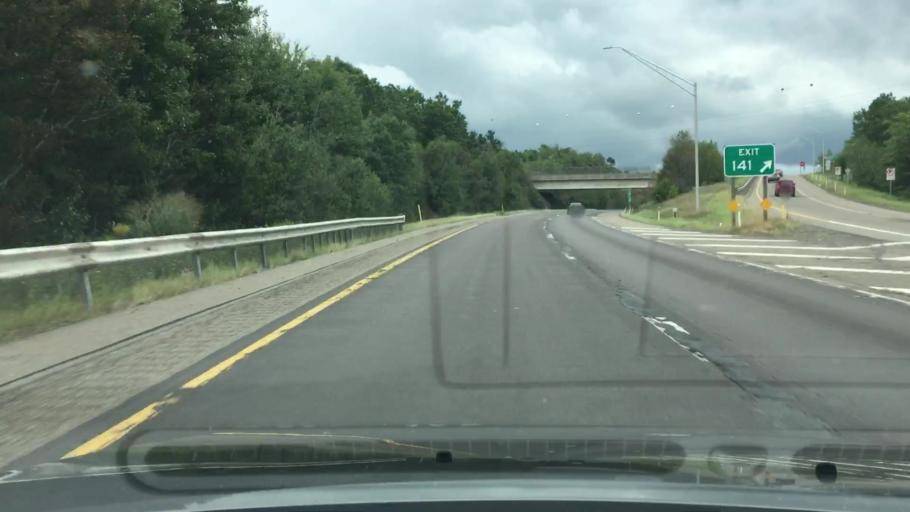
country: US
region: Pennsylvania
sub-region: Schuylkill County
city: McAdoo
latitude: 40.9275
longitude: -76.0124
